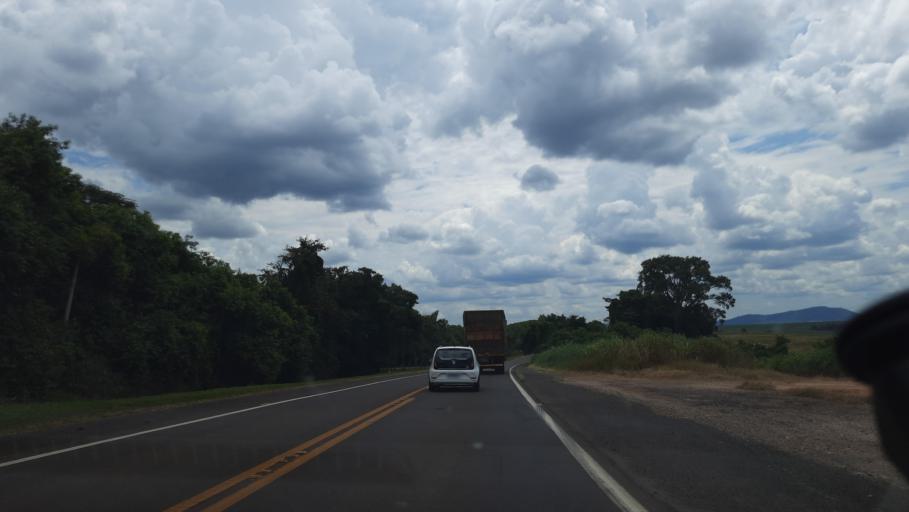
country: BR
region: Sao Paulo
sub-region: Mococa
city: Mococa
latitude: -21.4556
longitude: -47.1240
